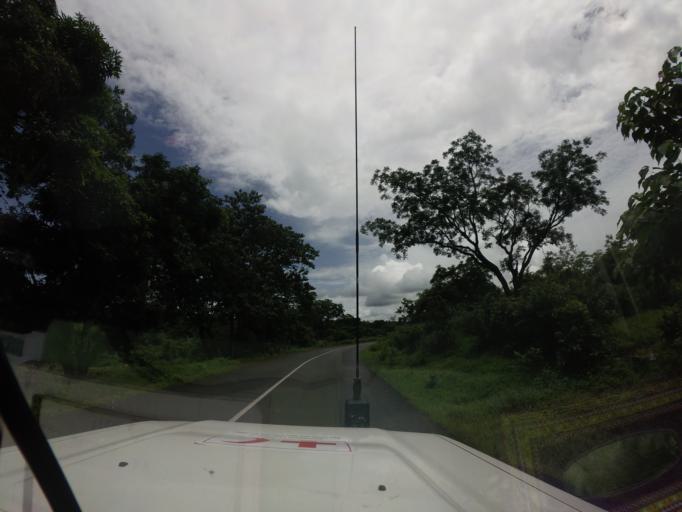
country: GN
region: Faranah
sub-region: Faranah Prefecture
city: Faranah
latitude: 10.0102
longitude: -10.9228
